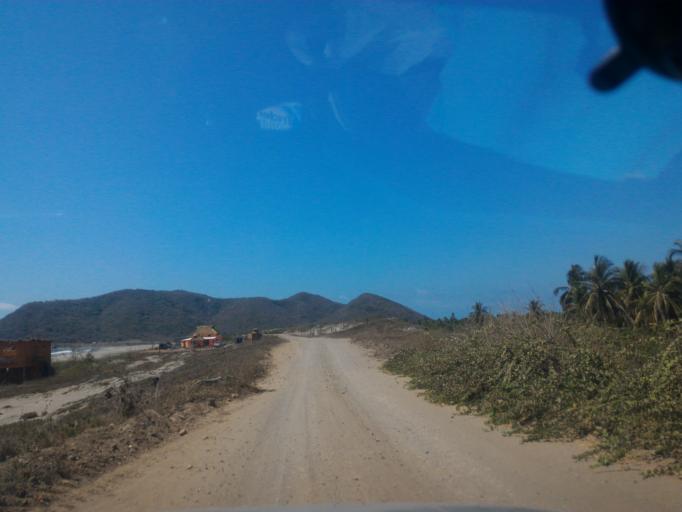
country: MX
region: Michoacan
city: Coahuayana Viejo
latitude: 18.5913
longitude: -103.6885
